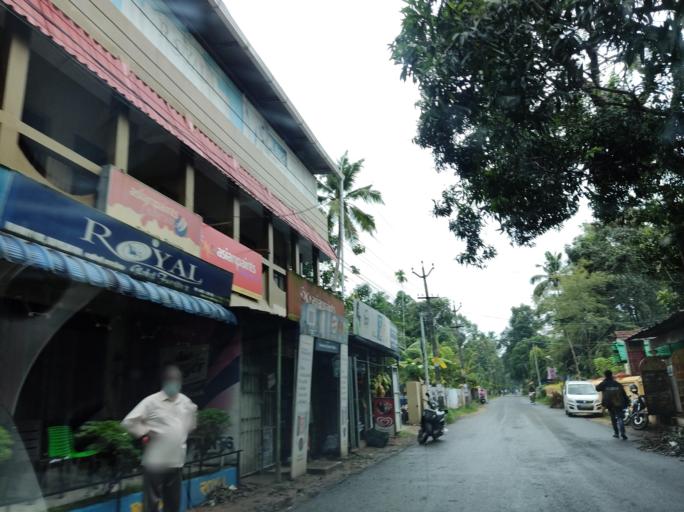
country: IN
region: Kerala
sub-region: Alappuzha
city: Mavelikara
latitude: 9.2508
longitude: 76.5296
